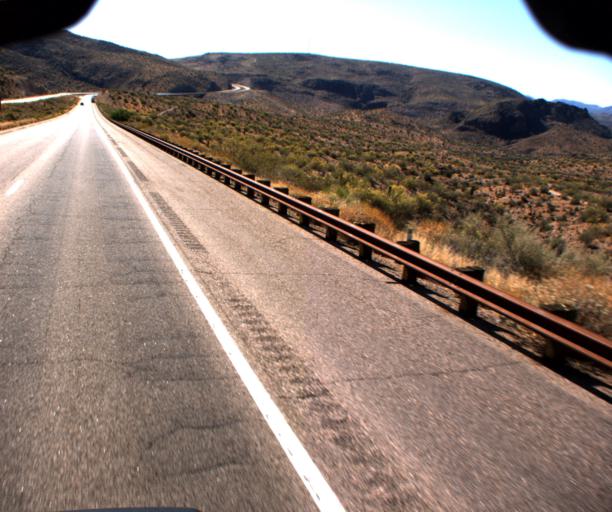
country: US
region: Arizona
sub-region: Yavapai County
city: Bagdad
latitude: 34.5842
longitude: -113.5028
